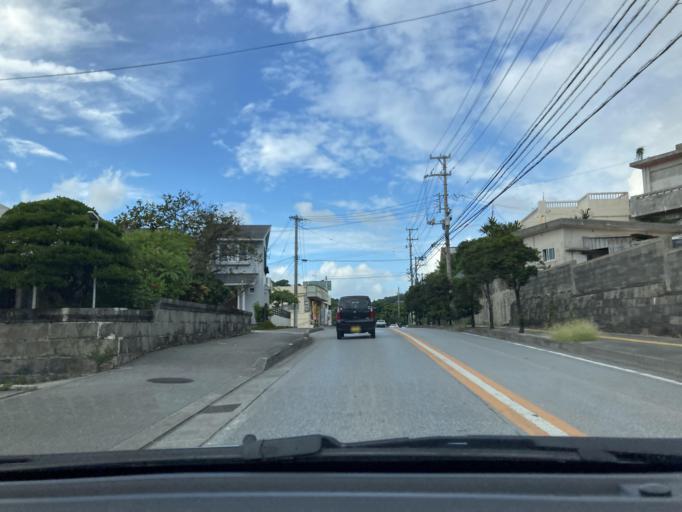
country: JP
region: Okinawa
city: Tomigusuku
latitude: 26.1814
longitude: 127.6852
